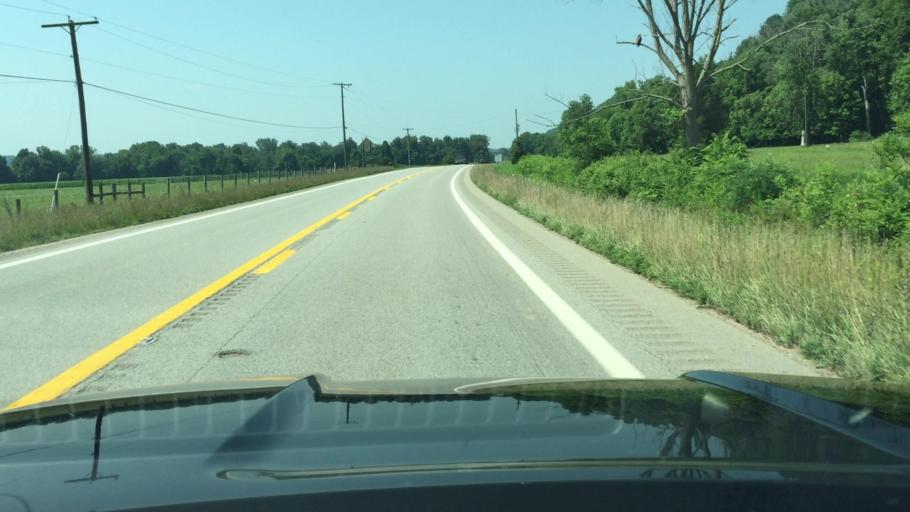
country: US
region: West Virginia
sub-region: Putnam County
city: Buffalo
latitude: 38.6310
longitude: -81.9793
